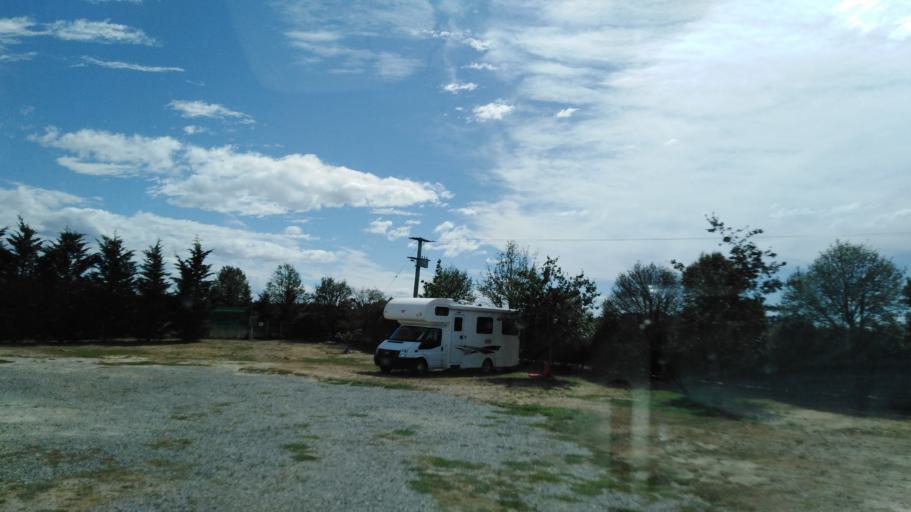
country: NZ
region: Canterbury
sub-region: Selwyn District
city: Rolleston
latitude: -43.5631
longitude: 172.4373
